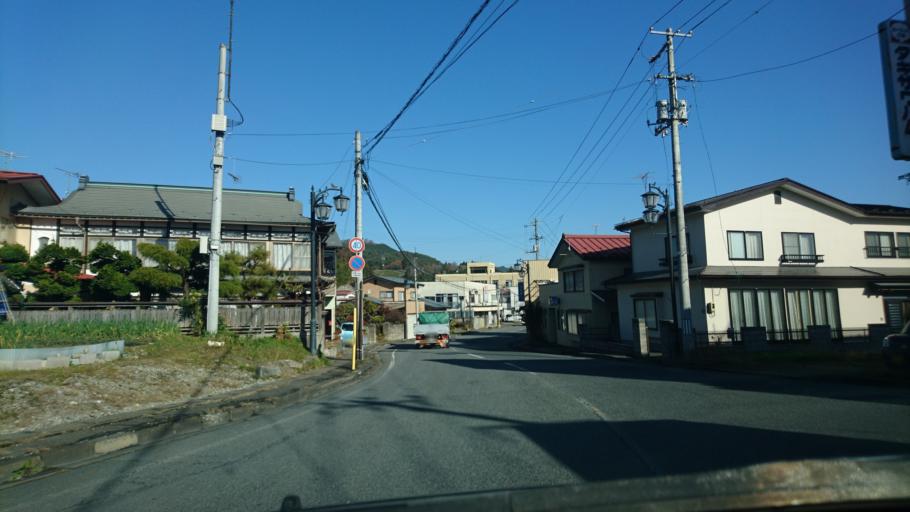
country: JP
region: Iwate
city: Ichinoseki
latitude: 38.9896
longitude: 141.2497
